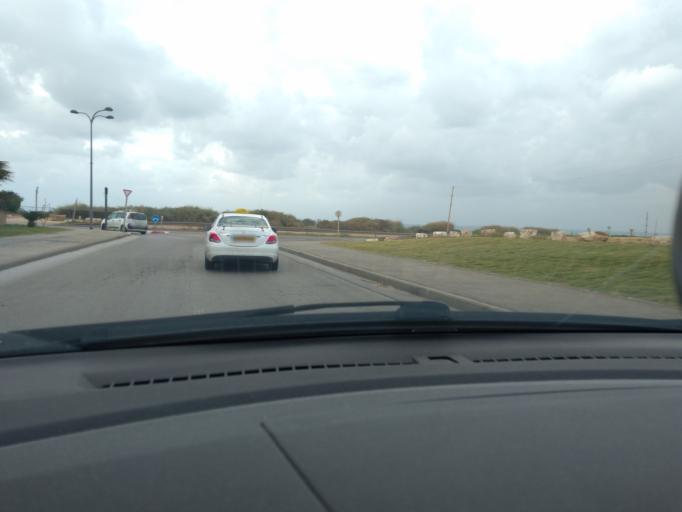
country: IL
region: Central District
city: Netanya
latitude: 32.3424
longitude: 34.8538
